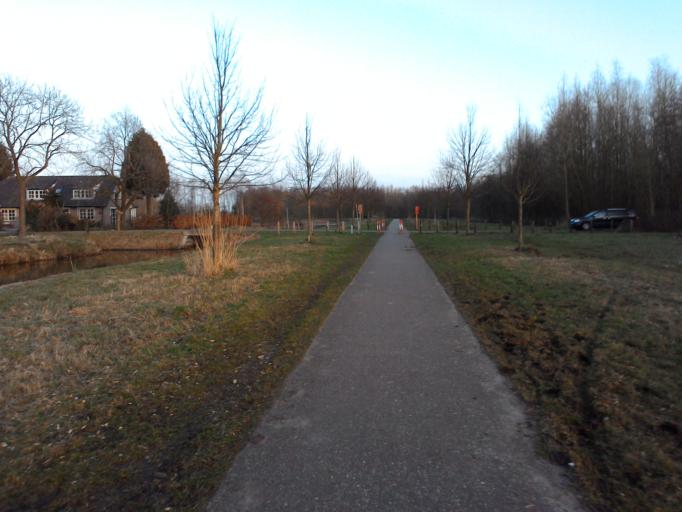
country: NL
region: Utrecht
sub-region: Gemeente Utrecht
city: Utrecht
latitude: 52.1250
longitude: 5.1203
